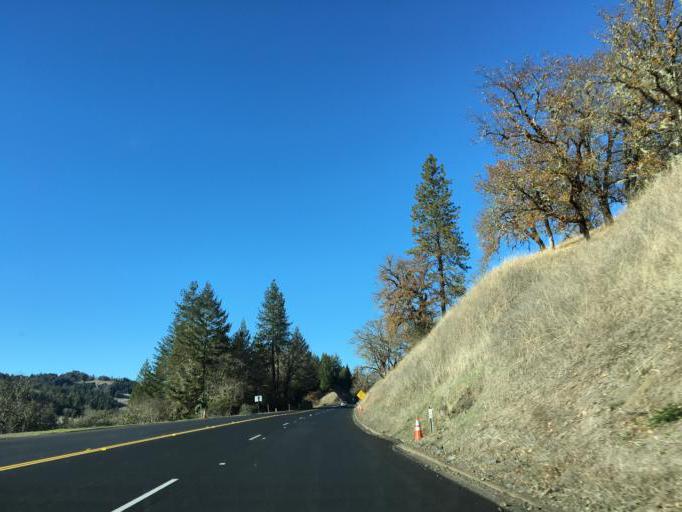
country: US
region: California
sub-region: Mendocino County
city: Laytonville
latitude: 39.7513
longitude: -123.5348
